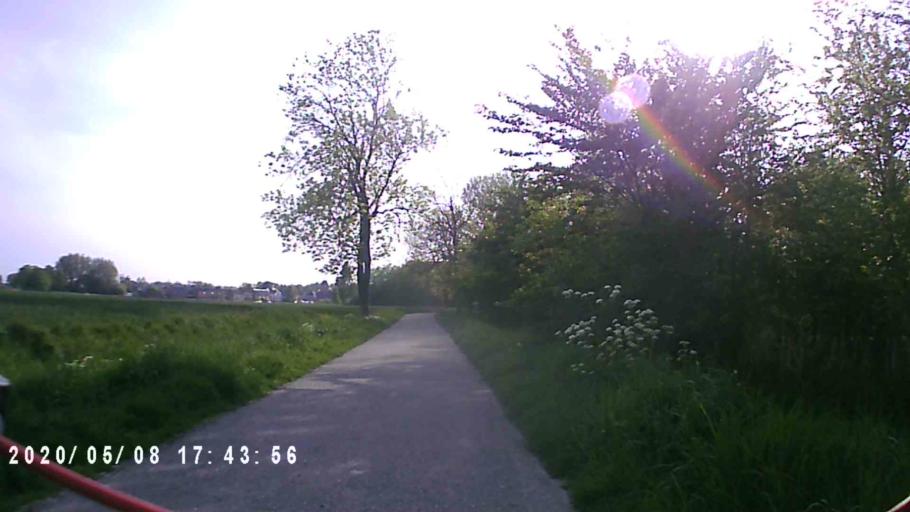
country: NL
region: Groningen
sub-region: Gemeente Winsum
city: Winsum
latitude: 53.3673
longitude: 6.5194
